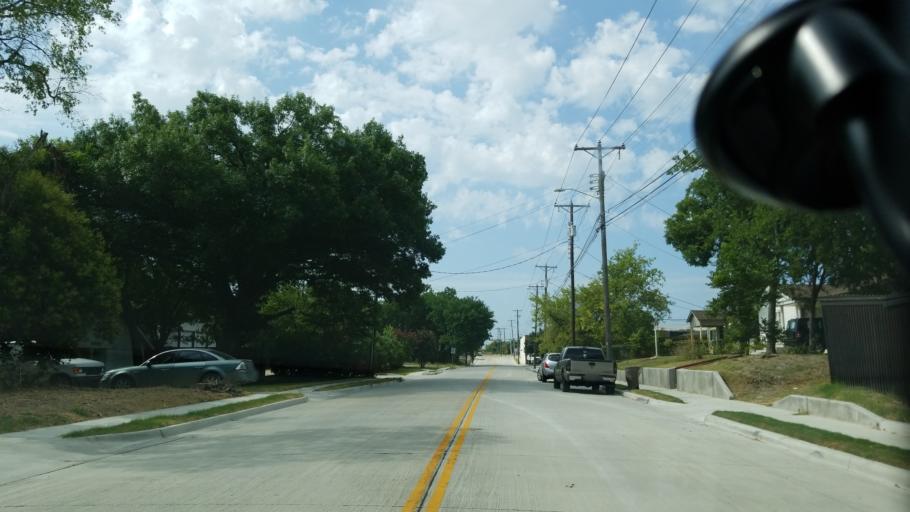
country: US
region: Texas
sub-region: Dallas County
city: Grand Prairie
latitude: 32.7481
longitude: -96.9982
